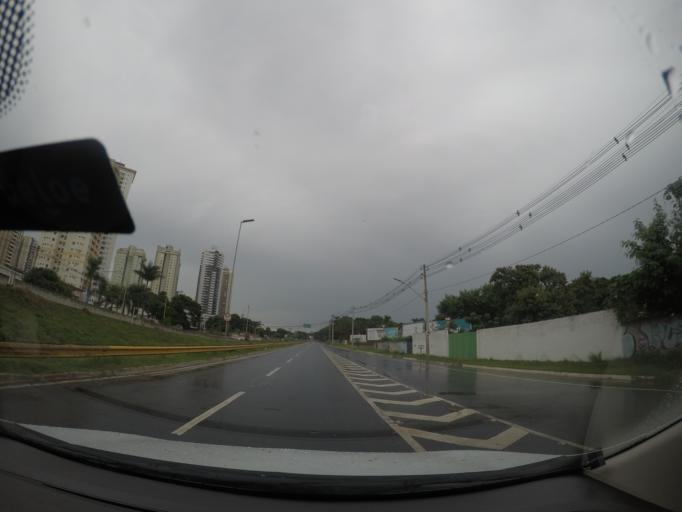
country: BR
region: Goias
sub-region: Goiania
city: Goiania
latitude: -16.6958
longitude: -49.2448
